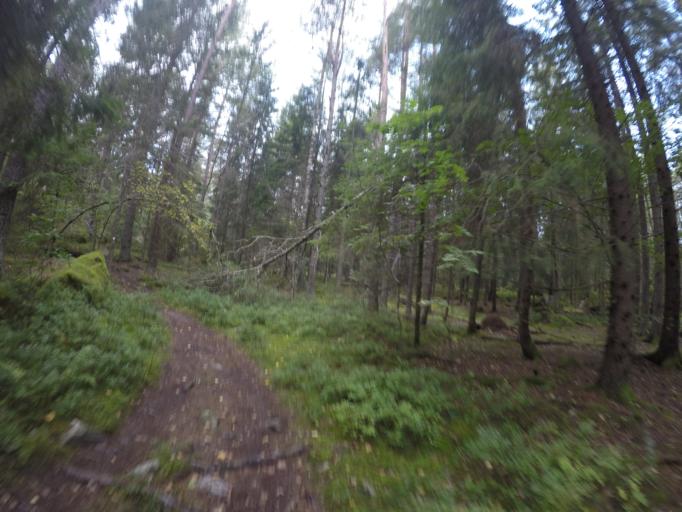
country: SE
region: Vaestmanland
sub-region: Vasteras
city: Vasteras
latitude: 59.6476
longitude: 16.5205
